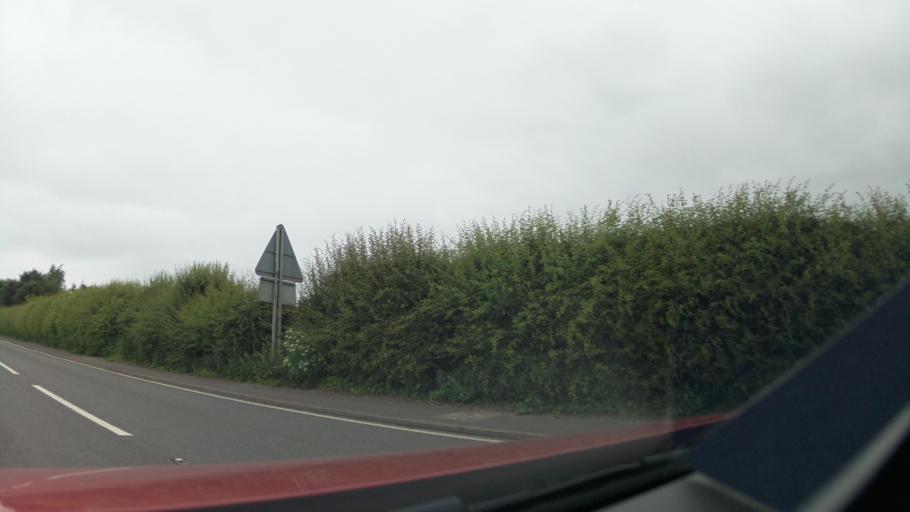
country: GB
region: England
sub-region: Derbyshire
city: Etwall
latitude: 52.9536
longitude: -1.5834
